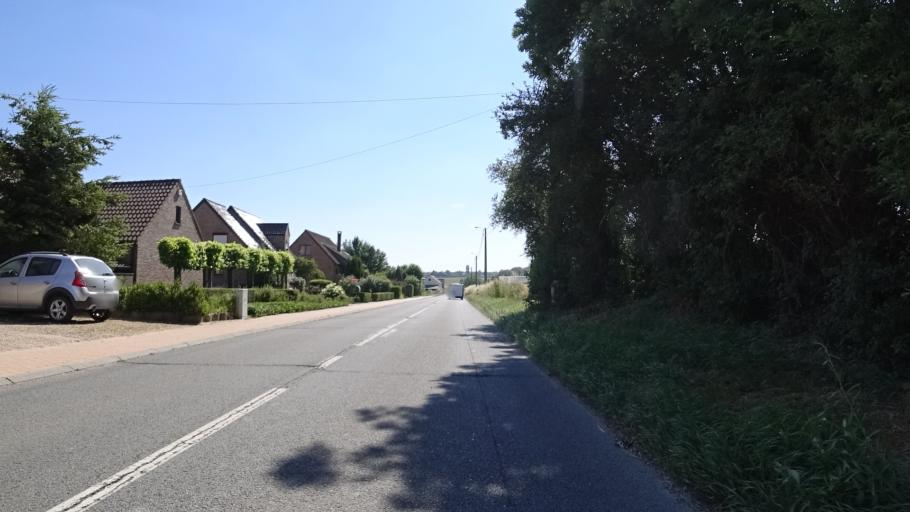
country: BE
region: Wallonia
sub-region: Province du Brabant Wallon
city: Jodoigne
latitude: 50.7206
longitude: 4.8604
